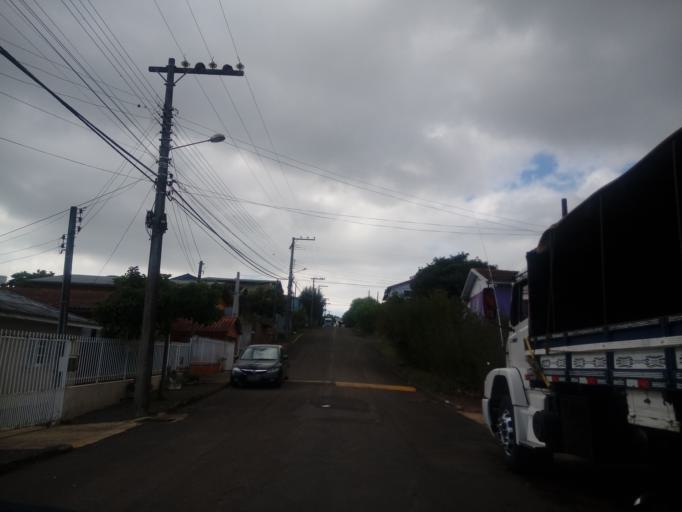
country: BR
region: Santa Catarina
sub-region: Chapeco
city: Chapeco
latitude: -27.1153
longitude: -52.6261
